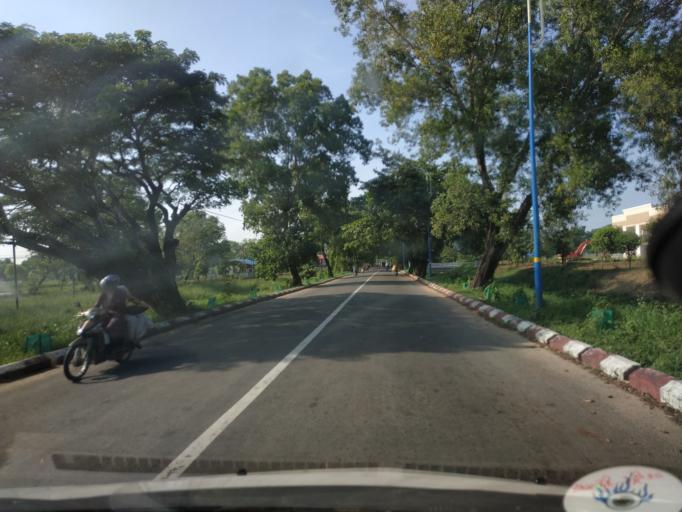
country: MM
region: Ayeyarwady
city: Pathein
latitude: 16.8109
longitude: 94.7549
